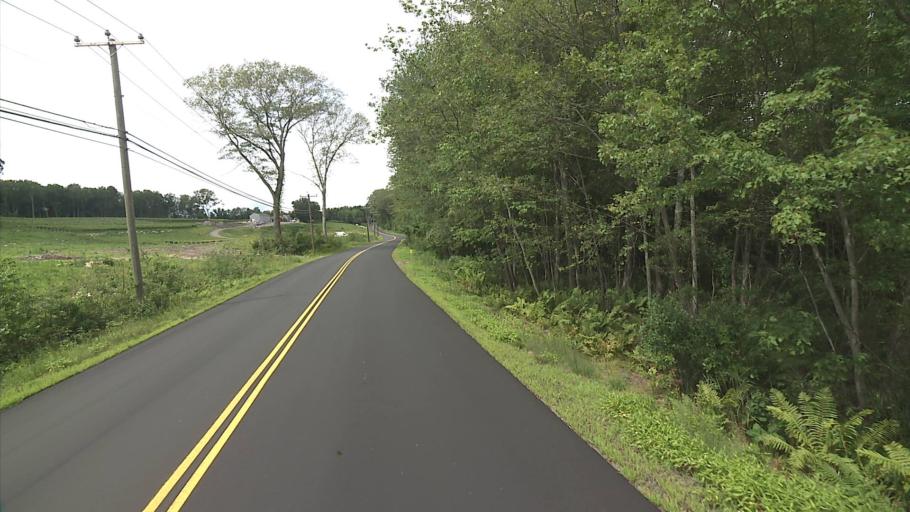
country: US
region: Connecticut
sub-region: Windham County
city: South Woodstock
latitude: 41.9445
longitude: -72.0053
